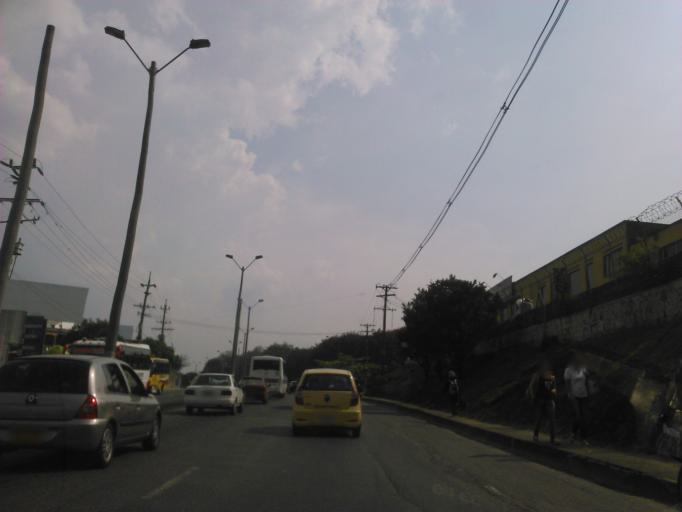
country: CO
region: Antioquia
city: Bello
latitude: 6.3090
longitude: -75.5600
